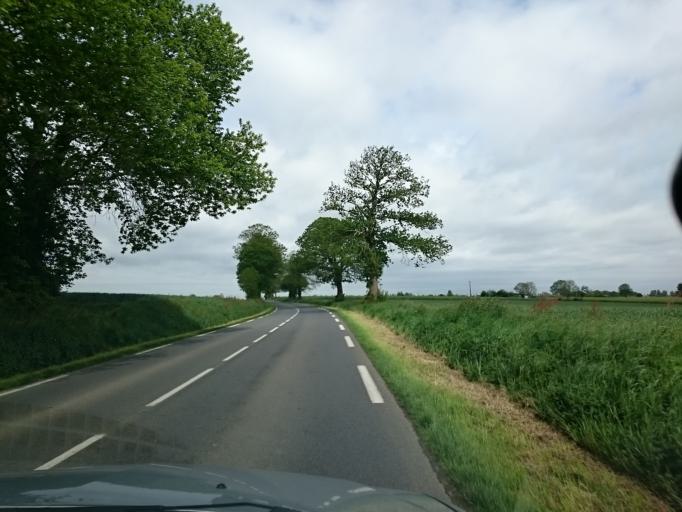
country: FR
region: Lower Normandy
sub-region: Departement de la Manche
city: Saint-James
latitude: 48.5407
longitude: -1.3654
